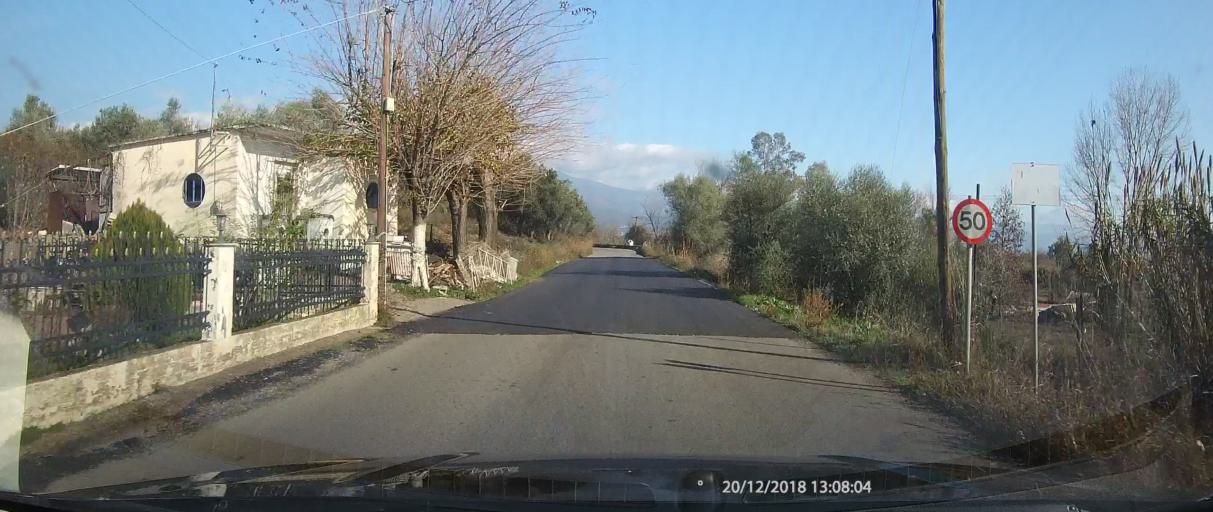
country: GR
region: West Greece
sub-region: Nomos Aitolias kai Akarnanias
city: Panaitolion
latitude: 38.5925
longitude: 21.4630
